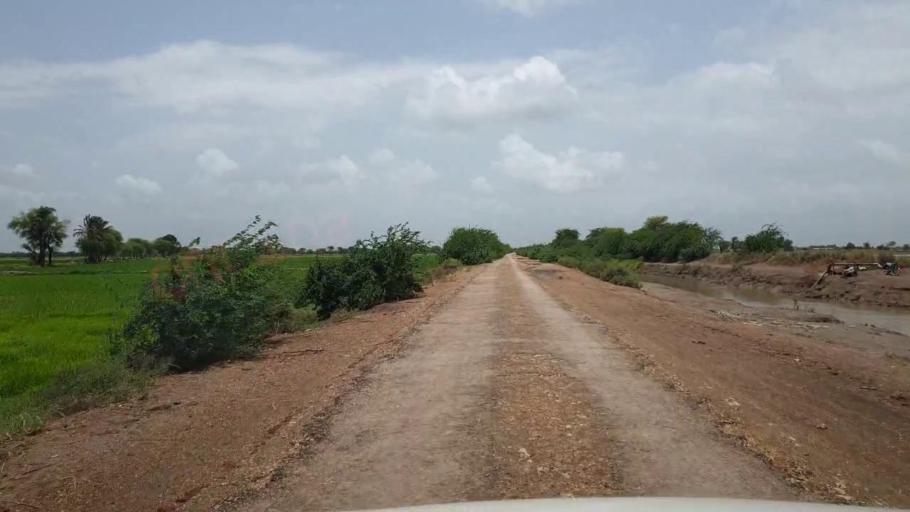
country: PK
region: Sindh
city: Kario
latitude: 24.7165
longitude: 68.5827
